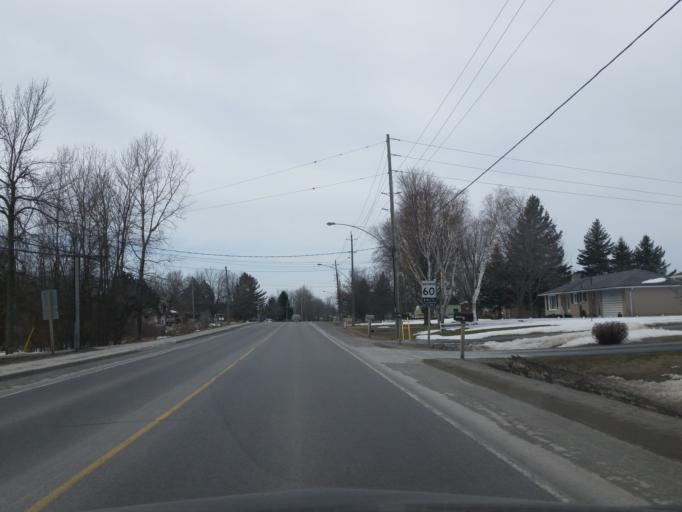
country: CA
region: Ontario
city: Skatepark
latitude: 44.2758
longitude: -76.7289
